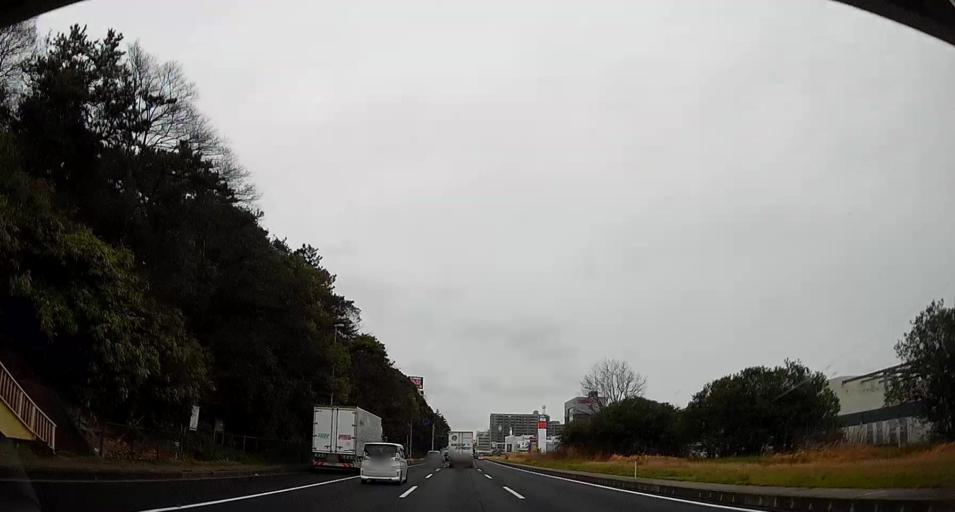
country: JP
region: Chiba
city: Chiba
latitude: 35.6228
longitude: 140.0940
